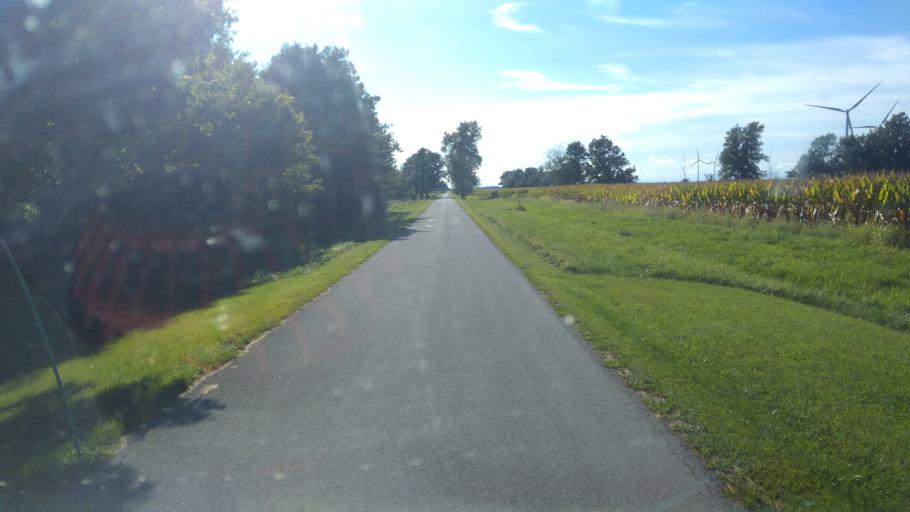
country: US
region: Ohio
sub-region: Hardin County
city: Ada
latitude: 40.7616
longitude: -83.7030
